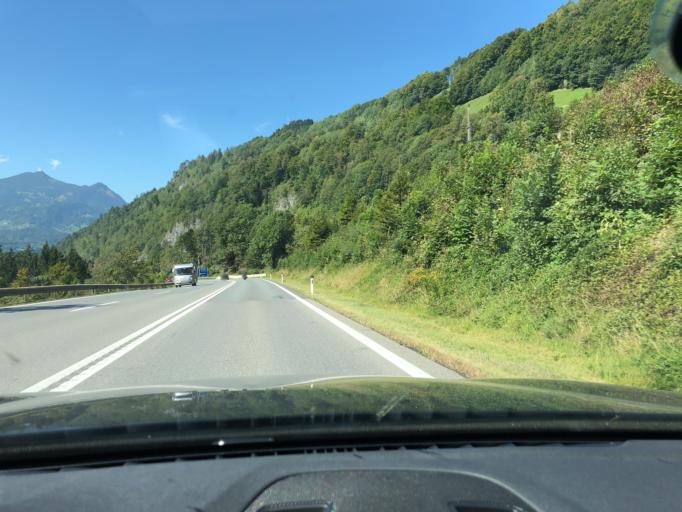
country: AT
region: Vorarlberg
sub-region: Politischer Bezirk Bludenz
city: Stallehr
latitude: 47.1432
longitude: 9.8703
